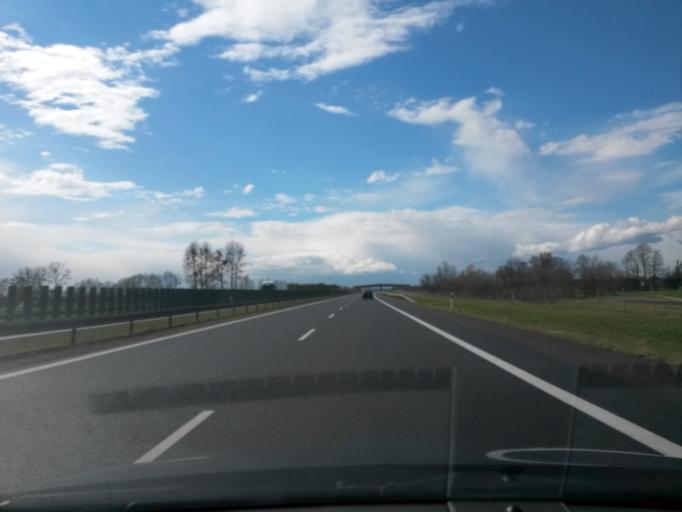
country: PL
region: Greater Poland Voivodeship
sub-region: Powiat slupecki
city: Strzalkowo
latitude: 52.2659
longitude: 17.7419
